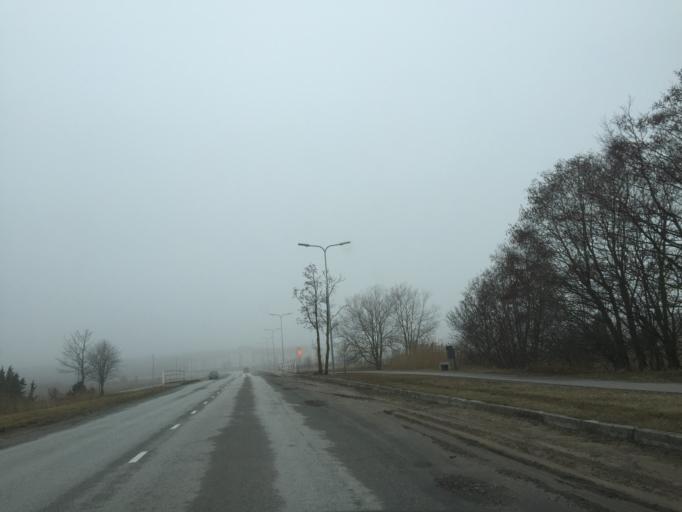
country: EE
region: Saare
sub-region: Kuressaare linn
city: Kuressaare
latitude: 58.2465
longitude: 22.4641
